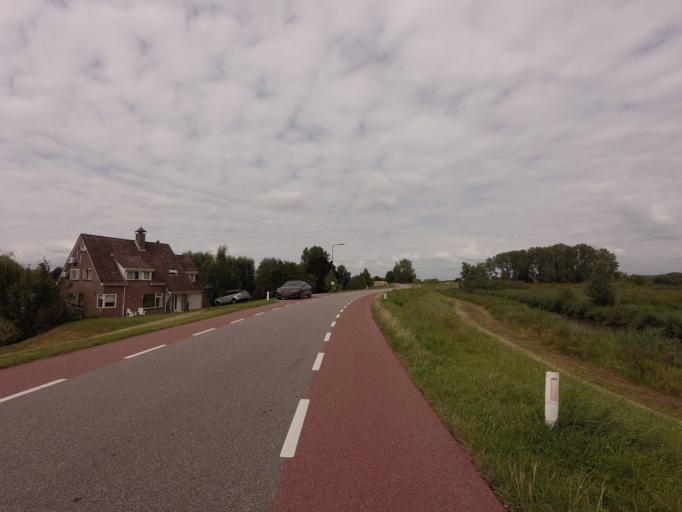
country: NL
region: South Holland
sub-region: Molenwaard
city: Liesveld
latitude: 51.9318
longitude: 4.8143
